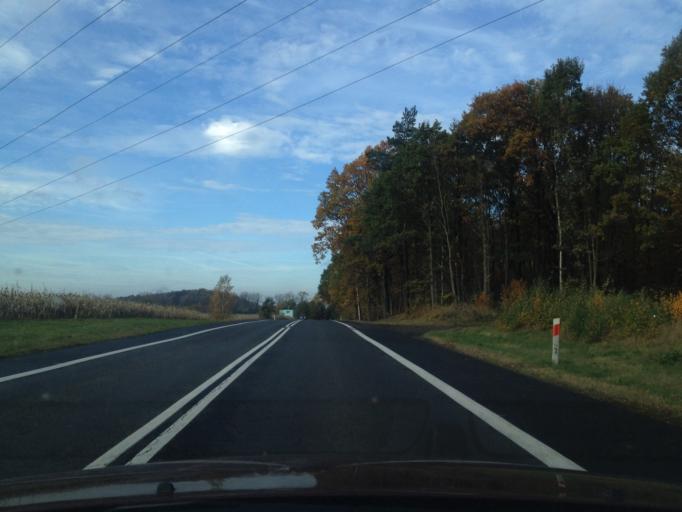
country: PL
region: Lower Silesian Voivodeship
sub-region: Powiat lubanski
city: Siekierczyn
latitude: 51.1463
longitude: 15.1861
